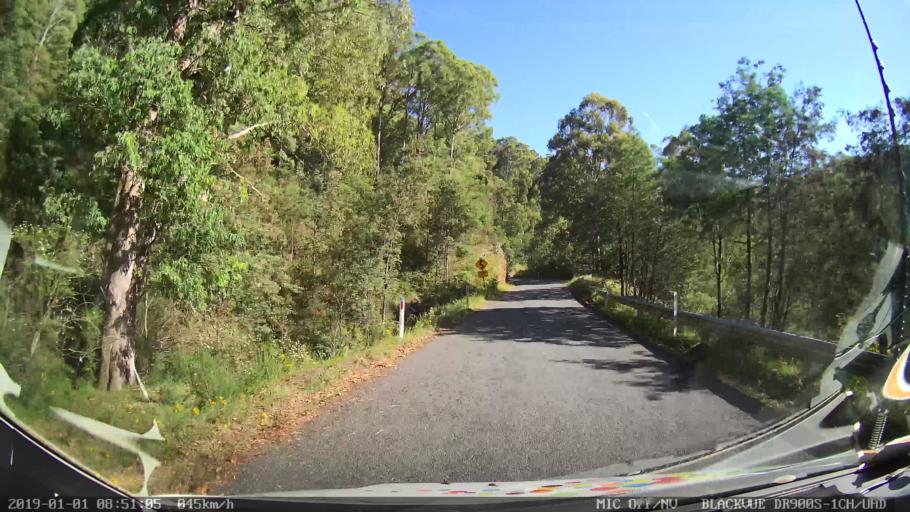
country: AU
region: New South Wales
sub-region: Snowy River
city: Jindabyne
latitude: -36.2731
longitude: 148.2002
